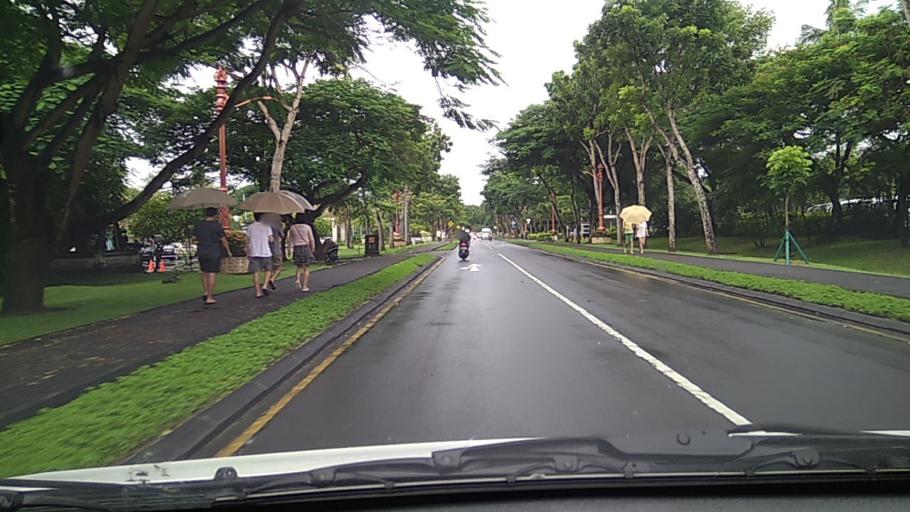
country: ID
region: Bali
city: Bualu
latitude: -8.8004
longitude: 115.2288
